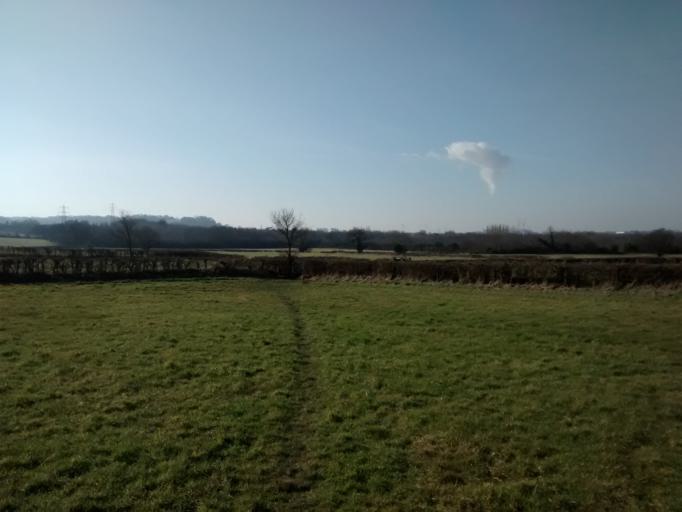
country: GB
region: England
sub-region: South Gloucestershire
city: Almondsbury
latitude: 51.5415
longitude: -2.6020
